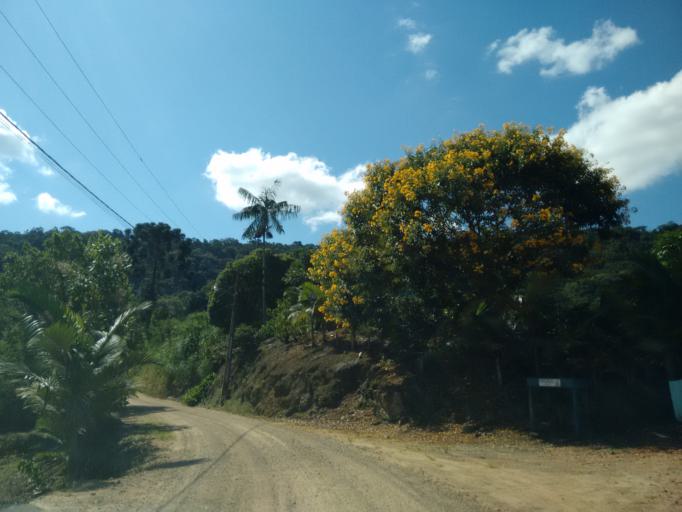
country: BR
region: Santa Catarina
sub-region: Indaial
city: Indaial
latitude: -26.9400
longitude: -49.1779
